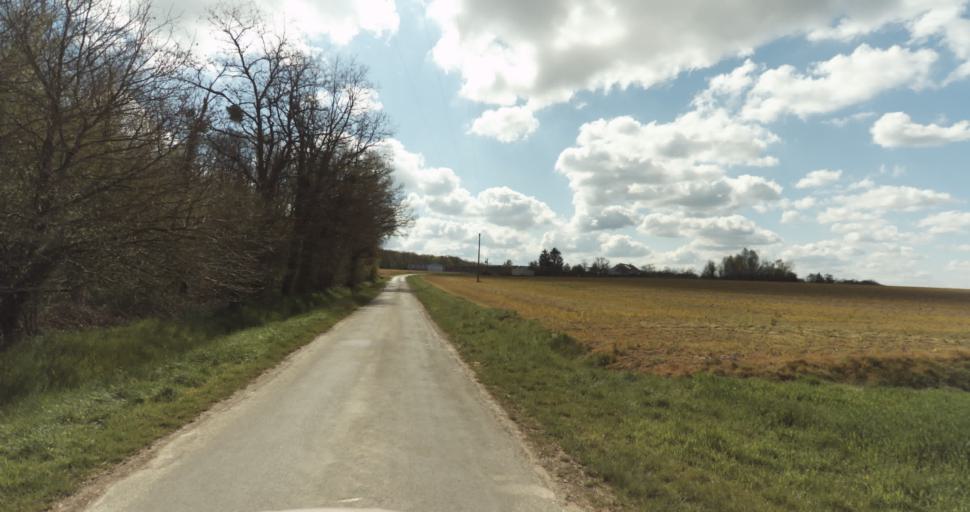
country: FR
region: Bourgogne
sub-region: Departement de la Cote-d'Or
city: Auxonne
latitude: 47.2128
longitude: 5.4312
